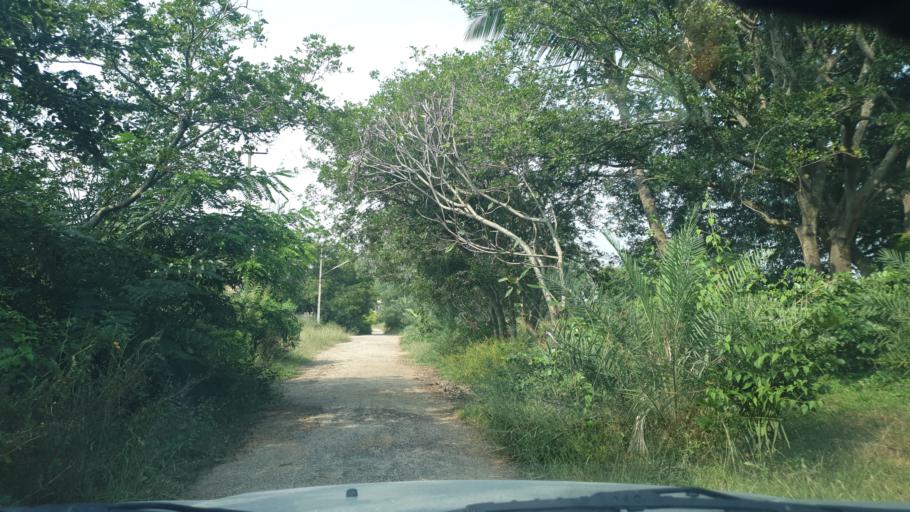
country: IN
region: Karnataka
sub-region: Bangalore Urban
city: Yelahanka
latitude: 13.0713
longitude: 77.6667
